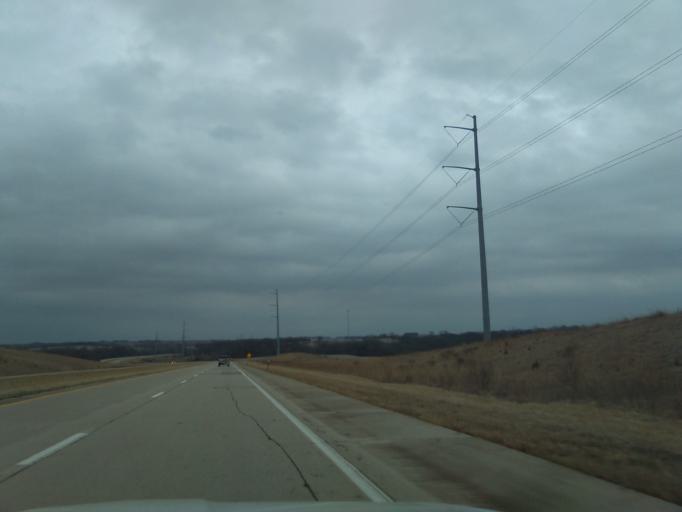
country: US
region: Nebraska
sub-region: Otoe County
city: Syracuse
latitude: 40.6755
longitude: -96.0485
